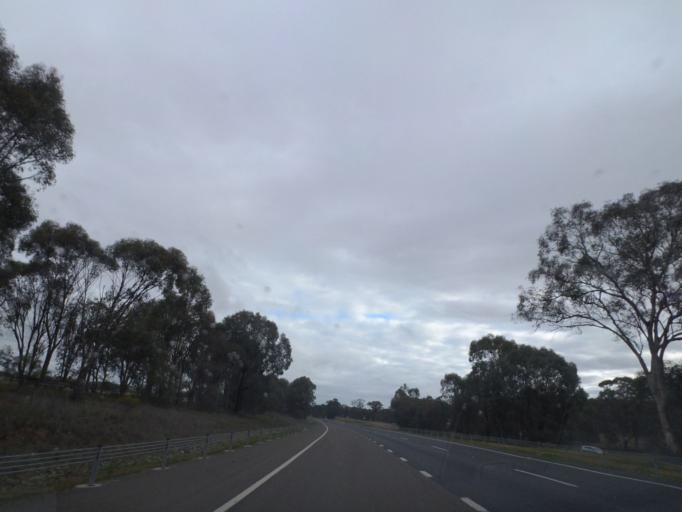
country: AU
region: Victoria
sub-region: Wangaratta
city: Wangaratta
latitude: -36.2241
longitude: 146.4442
